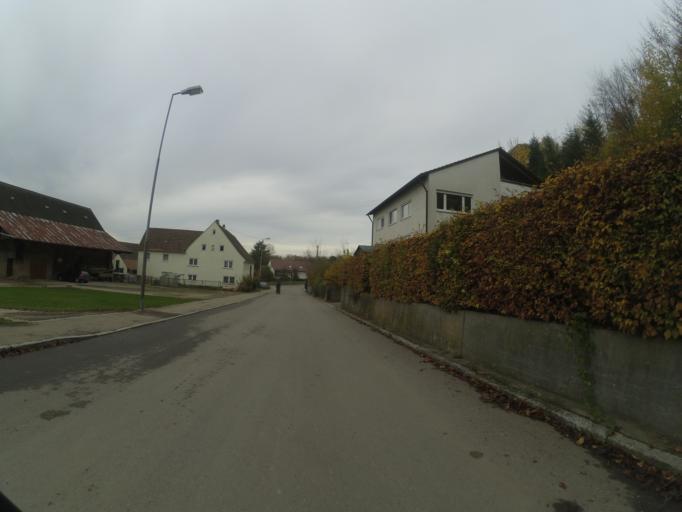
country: DE
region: Bavaria
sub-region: Swabia
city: Senden
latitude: 48.3392
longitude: 10.0063
